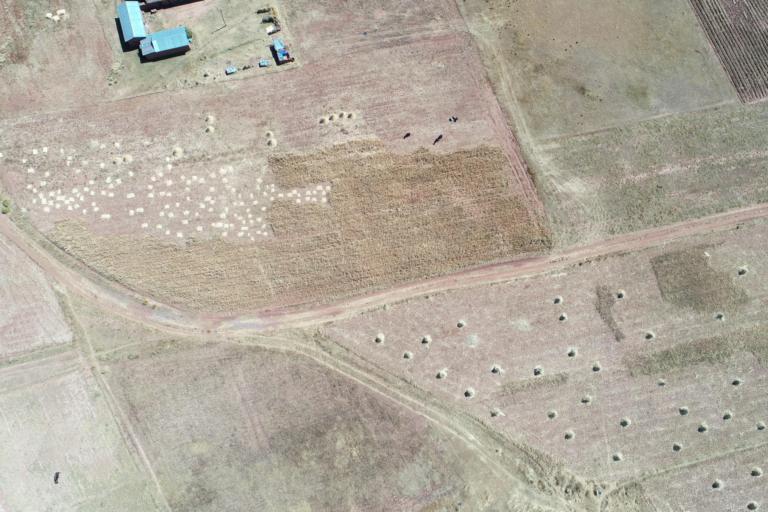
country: BO
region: La Paz
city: Tiahuanaco
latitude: -16.5874
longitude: -68.7695
